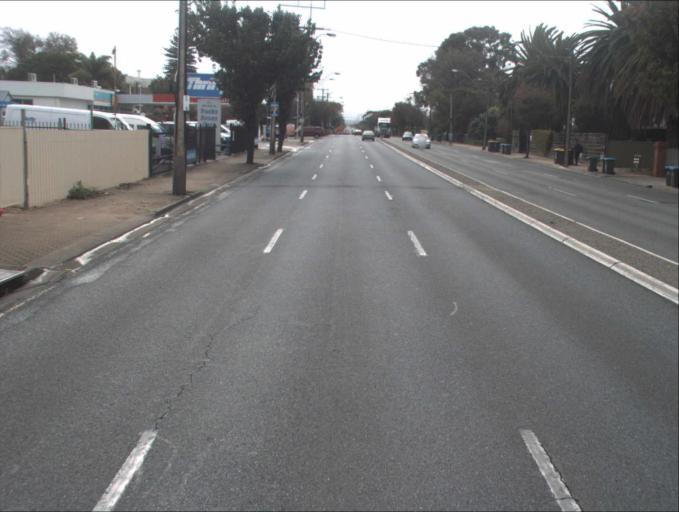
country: AU
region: South Australia
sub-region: Port Adelaide Enfield
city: Klemzig
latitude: -34.8873
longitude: 138.6159
